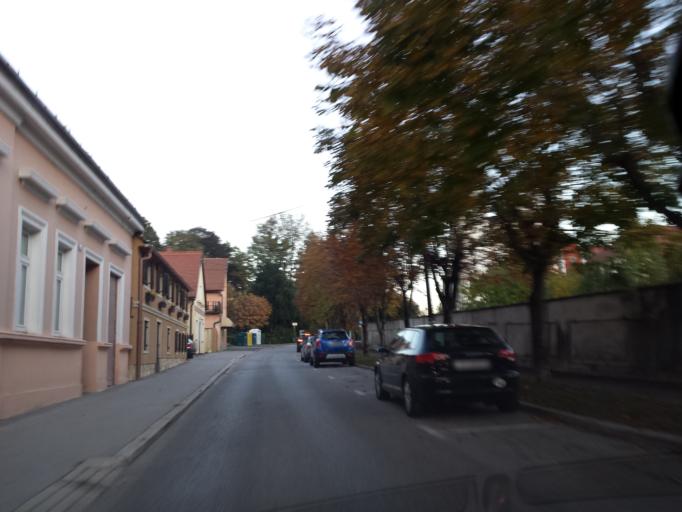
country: HR
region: Zagrebacka
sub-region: Grad Samobor
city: Samobor
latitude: 45.8006
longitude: 15.7123
